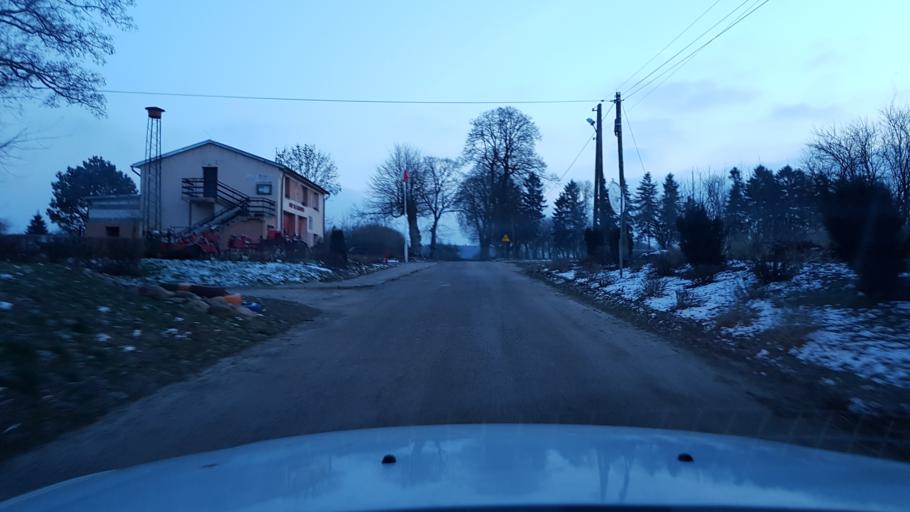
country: PL
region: West Pomeranian Voivodeship
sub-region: Powiat swidwinski
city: Slawoborze
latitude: 53.9472
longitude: 15.7239
